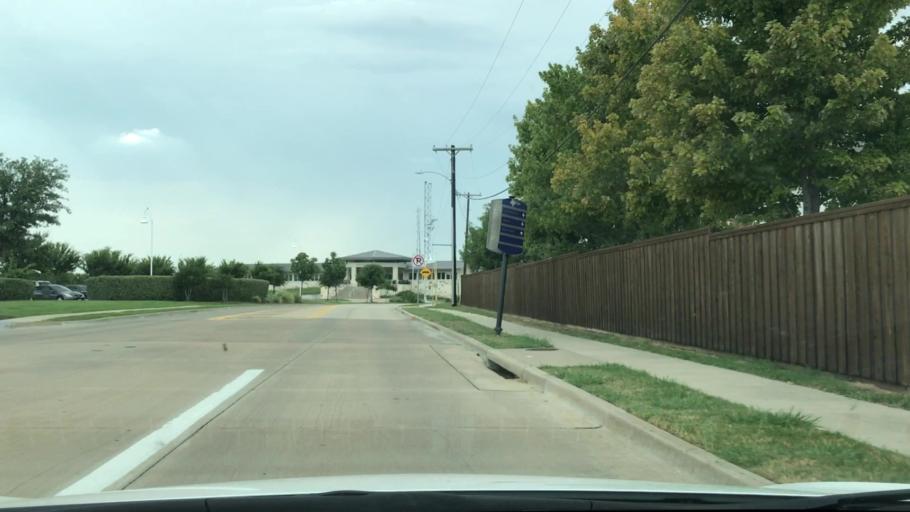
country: US
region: Texas
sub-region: Dallas County
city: Sachse
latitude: 32.9741
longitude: -96.5836
